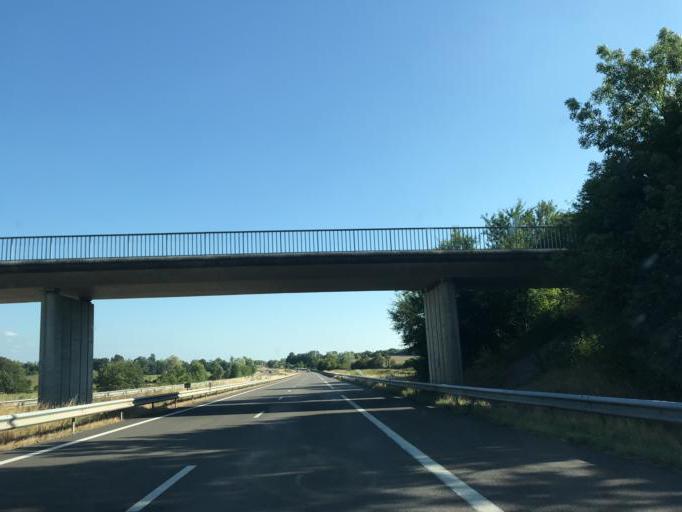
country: FR
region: Rhone-Alpes
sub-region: Departement de l'Ain
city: Marboz
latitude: 46.3843
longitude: 5.2706
